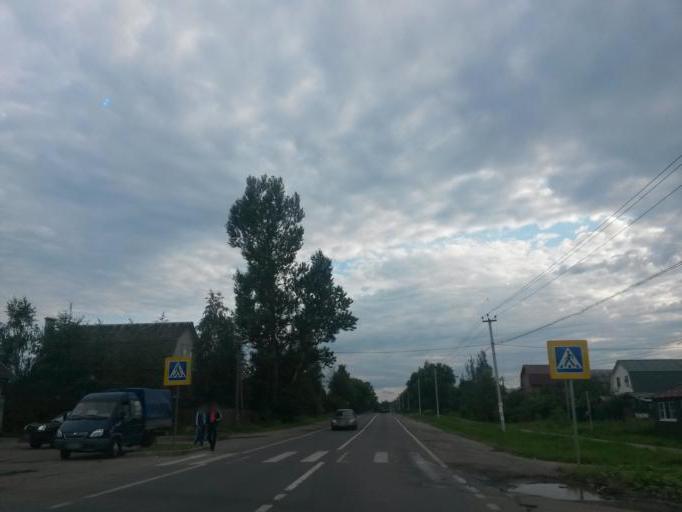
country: RU
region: Moskovskaya
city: Vostryakovo
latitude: 55.4037
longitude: 37.8184
